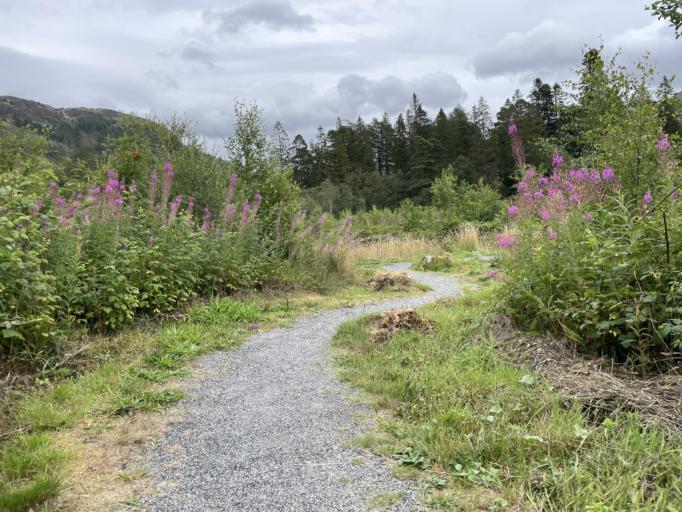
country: GB
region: Scotland
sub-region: Dumfries and Galloway
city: Newton Stewart
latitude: 55.0874
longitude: -4.5053
